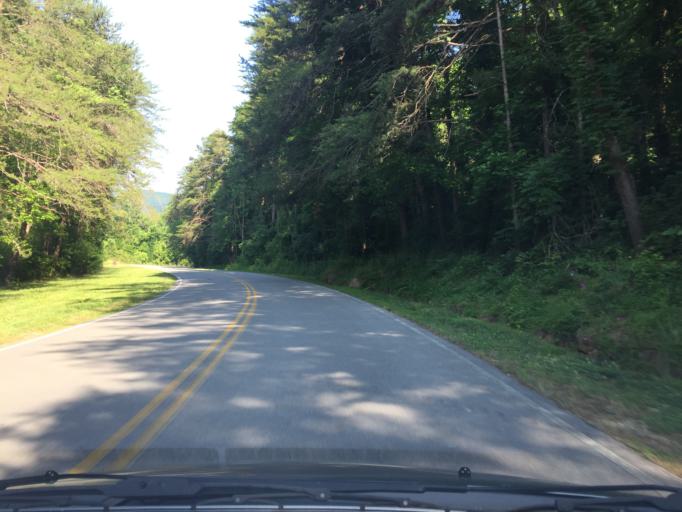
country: US
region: Tennessee
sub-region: Hamilton County
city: Lookout Mountain
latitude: 35.0389
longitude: -85.4185
